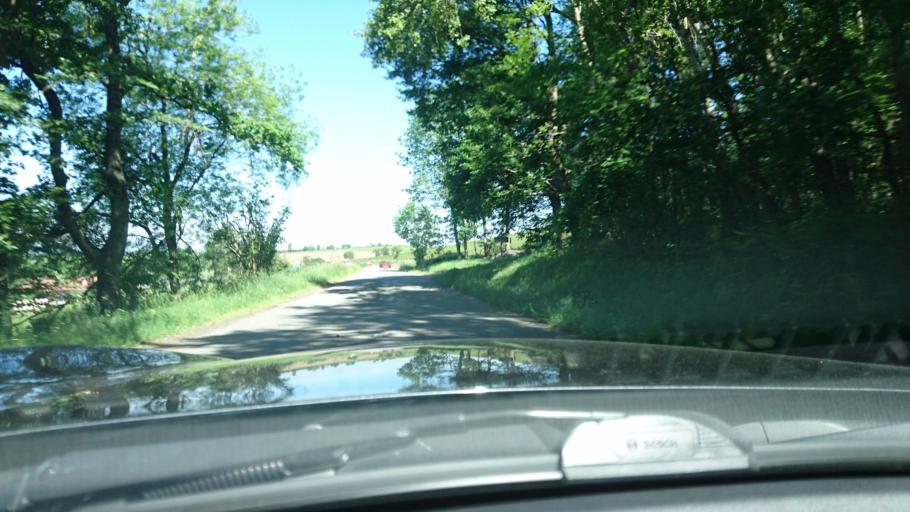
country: FR
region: Rhone-Alpes
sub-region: Departement de la Loire
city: Violay
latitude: 45.8987
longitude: 4.3155
